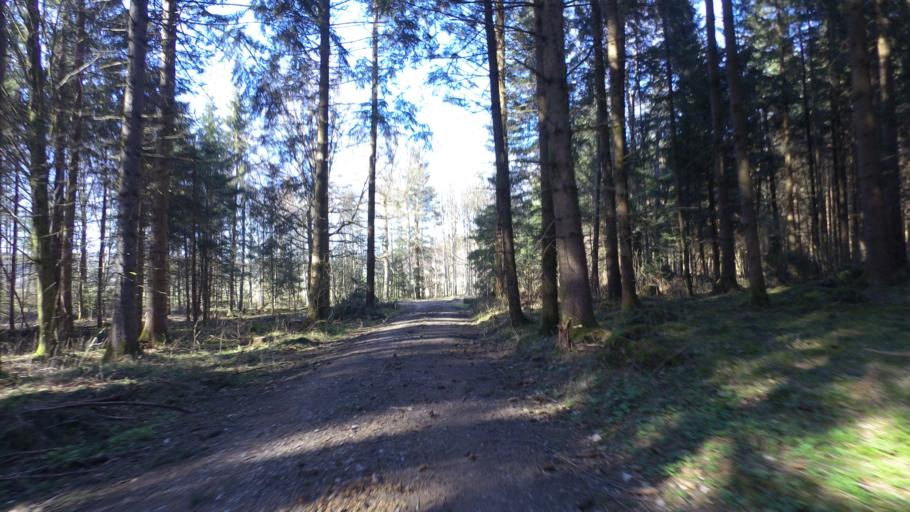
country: DE
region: Bavaria
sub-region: Upper Bavaria
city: Chieming
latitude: 47.9363
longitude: 12.5364
